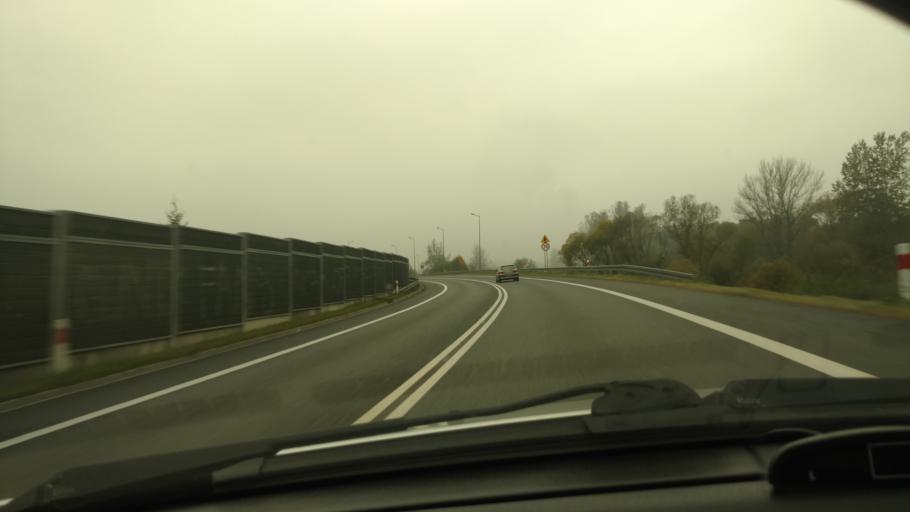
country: PL
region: Lesser Poland Voivodeship
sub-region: Powiat gorlicki
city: Biecz
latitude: 49.7102
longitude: 21.2416
